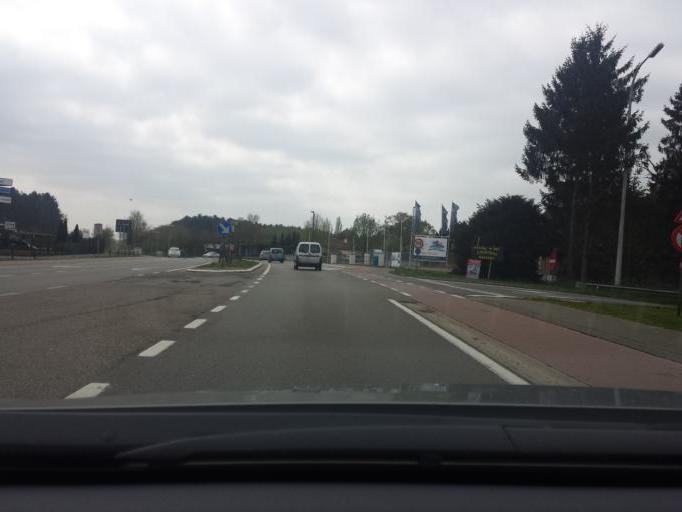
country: BE
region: Flanders
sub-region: Provincie Limburg
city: Lummen
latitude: 50.9949
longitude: 5.1972
